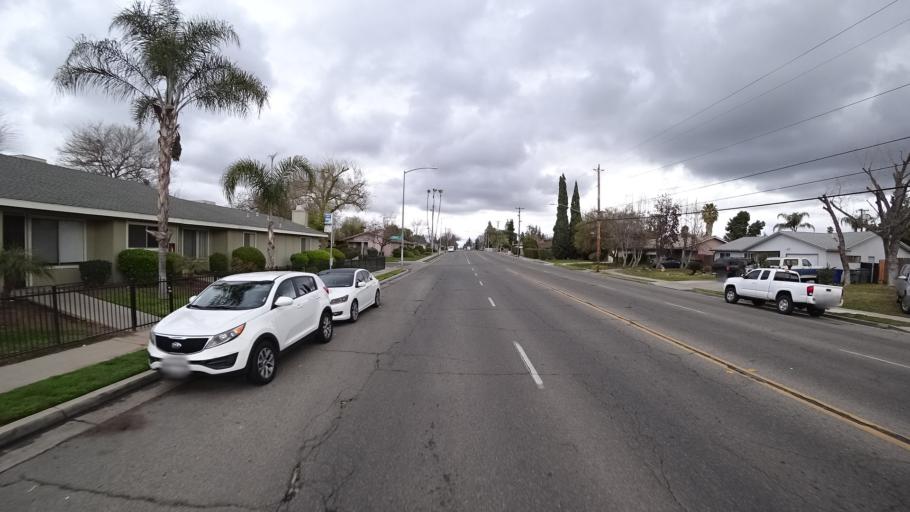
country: US
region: California
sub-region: Fresno County
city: West Park
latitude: 36.7893
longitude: -119.8444
